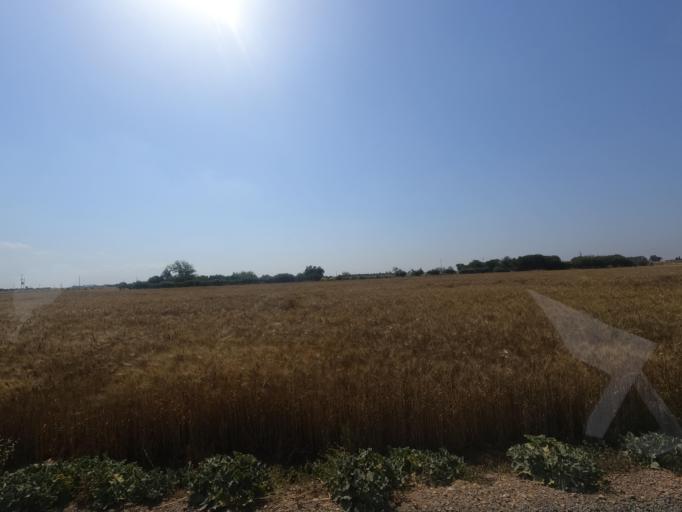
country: CY
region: Ammochostos
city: Avgorou
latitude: 35.0527
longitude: 33.8537
